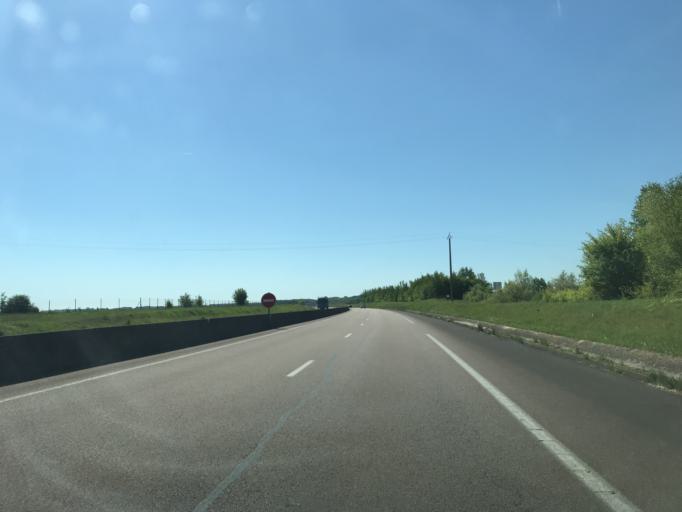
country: FR
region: Haute-Normandie
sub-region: Departement de l'Eure
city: La Madeleine-de-Nonancourt
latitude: 48.8350
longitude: 1.1831
